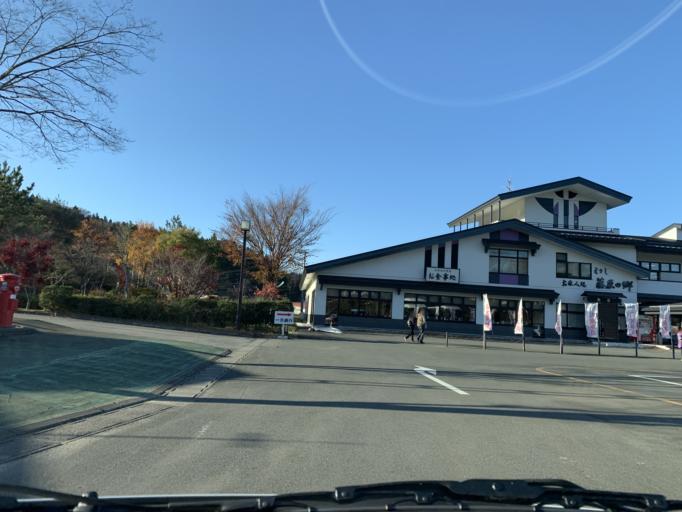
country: JP
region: Iwate
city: Mizusawa
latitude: 39.1967
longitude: 141.1892
